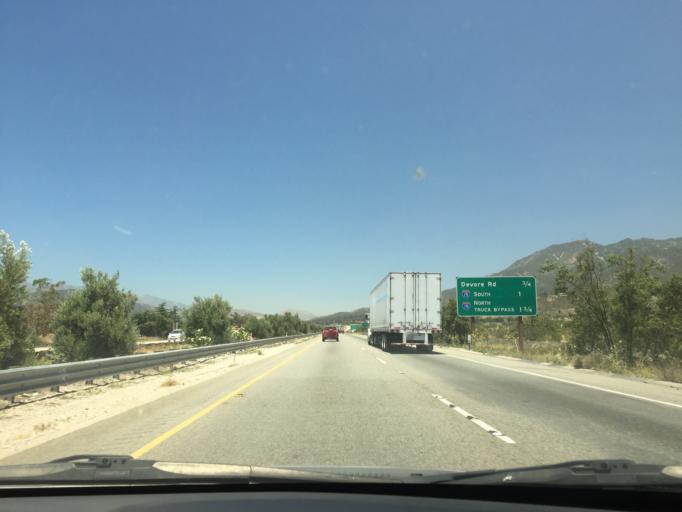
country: US
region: California
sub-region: San Bernardino County
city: Muscoy
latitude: 34.2126
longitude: -117.3891
